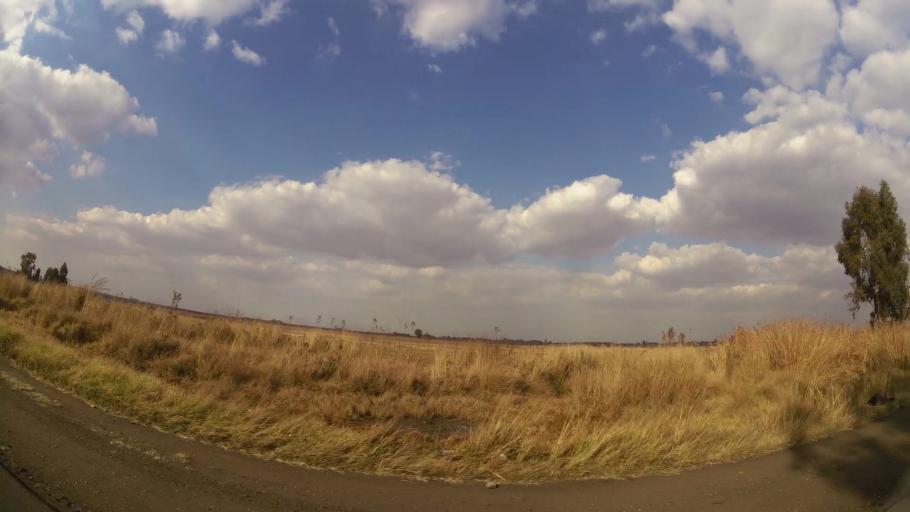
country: ZA
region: Mpumalanga
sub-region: Nkangala District Municipality
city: Delmas
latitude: -26.1610
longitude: 28.6974
